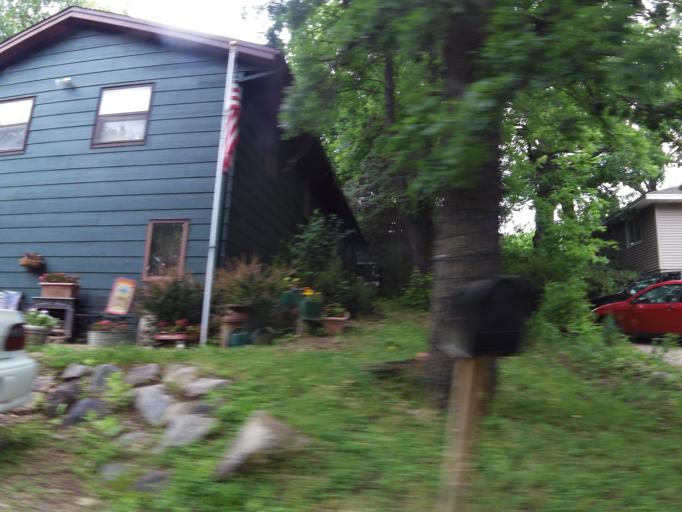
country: US
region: Minnesota
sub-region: Scott County
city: Prior Lake
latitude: 44.7088
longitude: -93.4426
